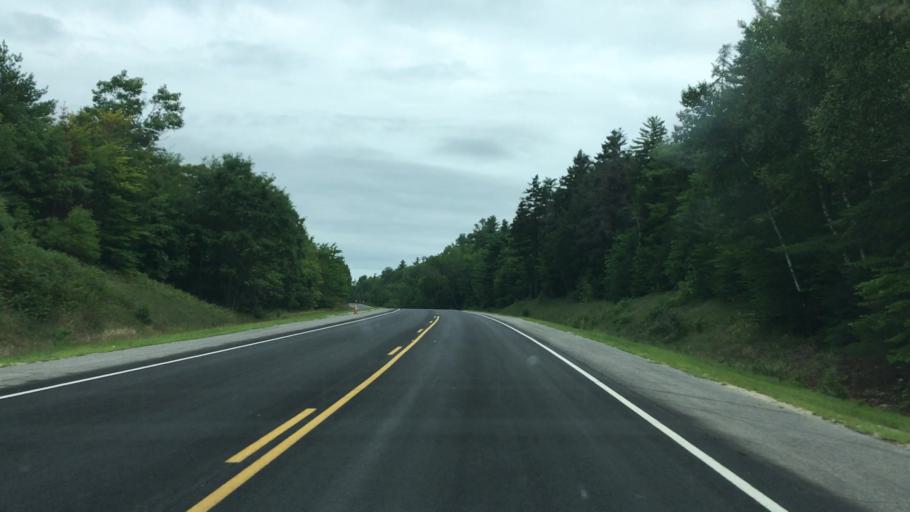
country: US
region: Maine
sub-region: Washington County
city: Cherryfield
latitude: 44.8977
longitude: -67.8557
